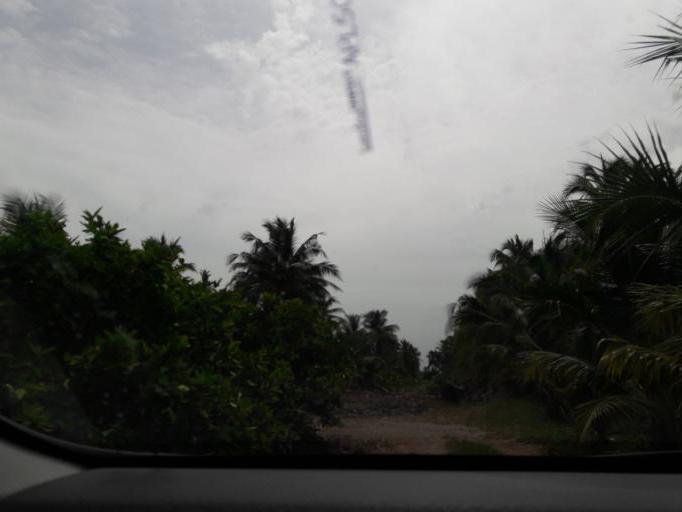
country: TH
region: Ratchaburi
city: Damnoen Saduak
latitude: 13.5621
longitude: 99.9950
